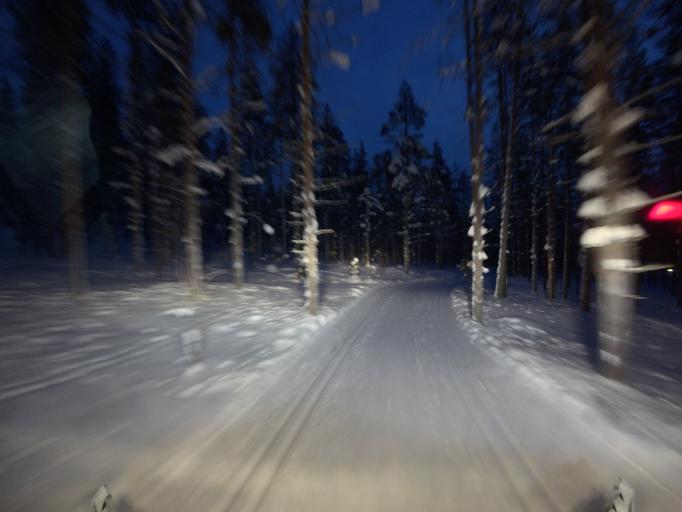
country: FI
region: Lapland
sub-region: Tunturi-Lappi
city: Kolari
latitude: 67.6027
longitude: 24.1253
